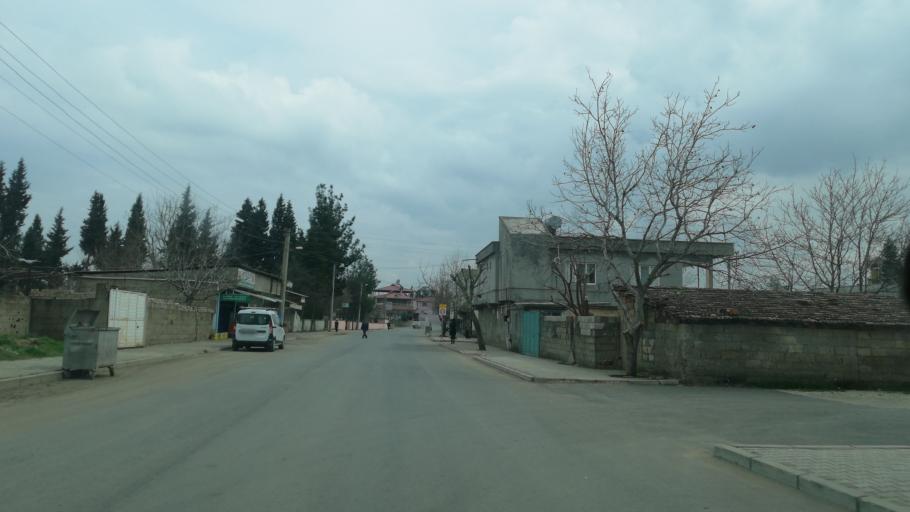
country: TR
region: Kahramanmaras
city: Turkoglu
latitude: 37.4114
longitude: 36.8831
